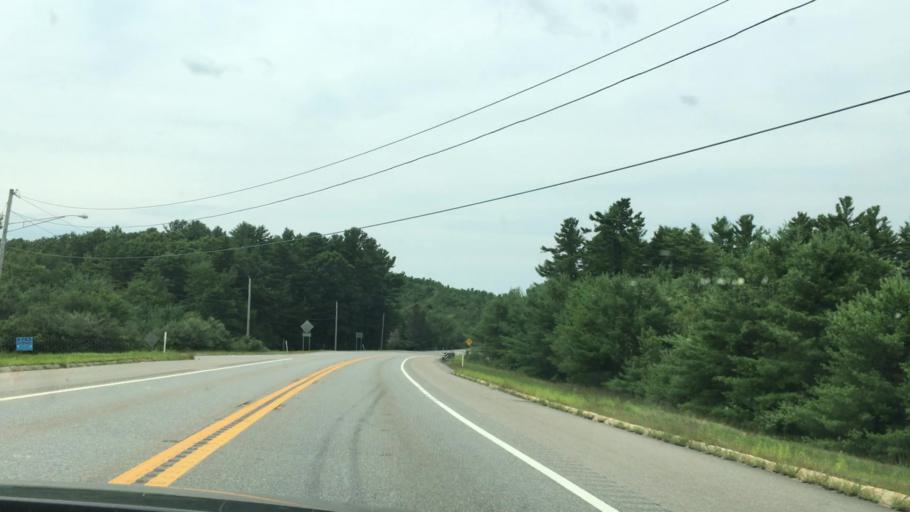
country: US
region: Massachusetts
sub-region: Worcester County
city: Gardner
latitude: 42.6045
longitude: -71.9894
